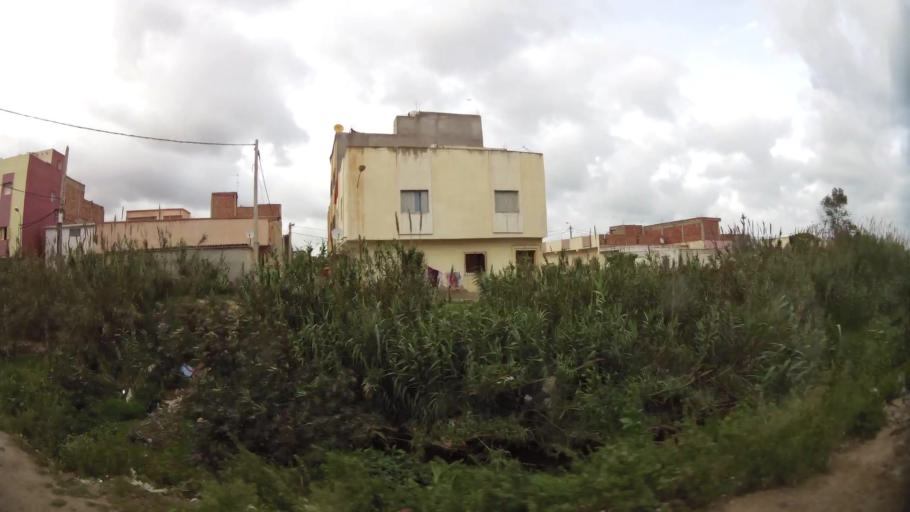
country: MA
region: Oriental
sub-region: Nador
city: Nador
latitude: 35.1599
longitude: -2.9129
